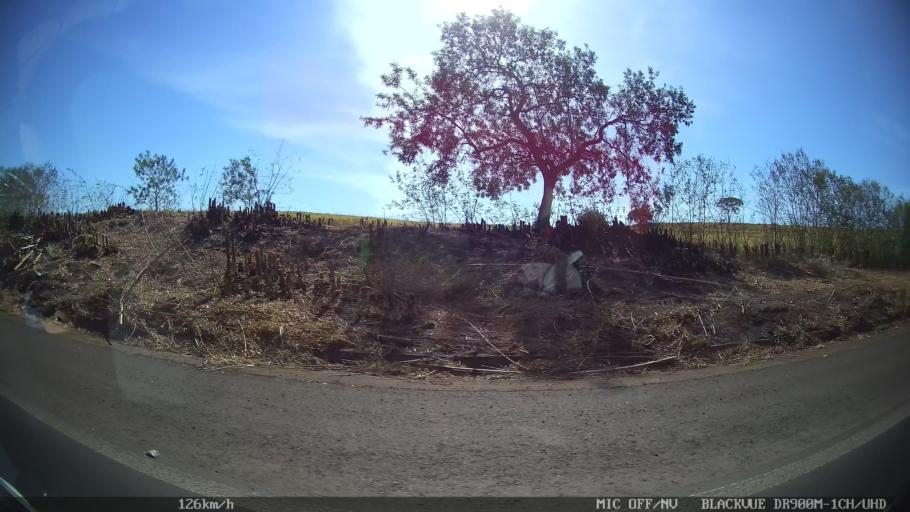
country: BR
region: Sao Paulo
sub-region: Barretos
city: Barretos
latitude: -20.5832
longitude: -48.6941
